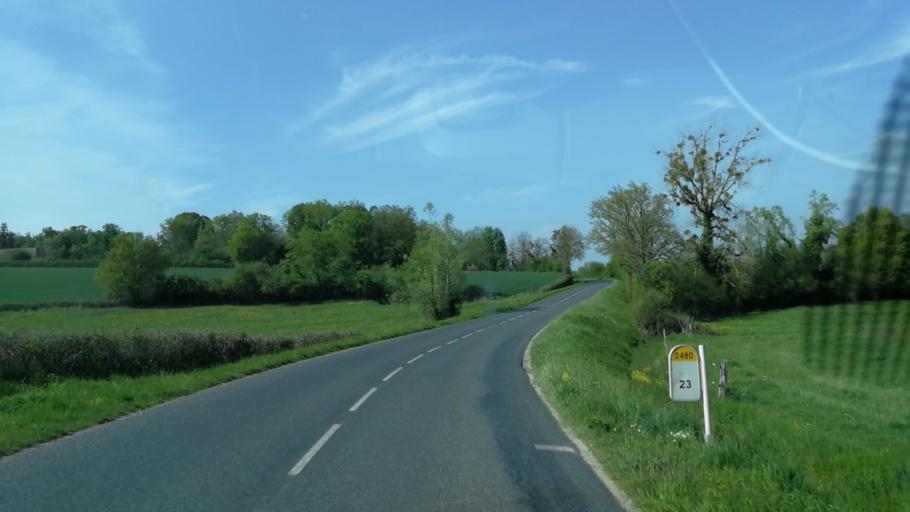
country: FR
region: Auvergne
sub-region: Departement de l'Allier
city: Saint-Gerand-le-Puy
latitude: 46.3431
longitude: 3.5788
